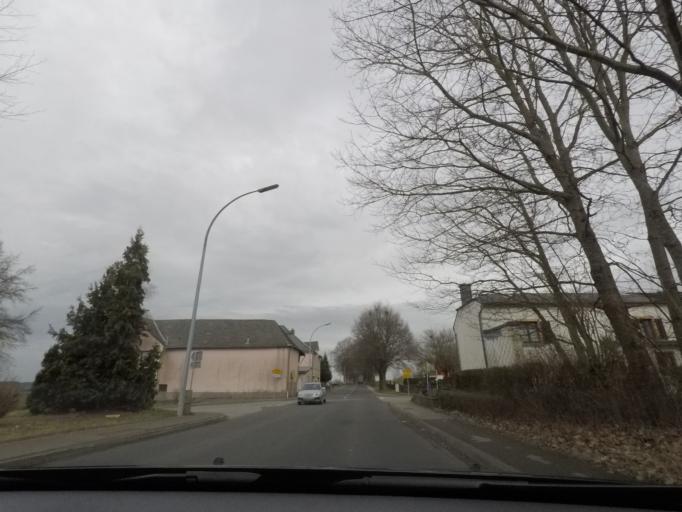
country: LU
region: Diekirch
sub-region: Canton de Wiltz
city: Winseler
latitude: 50.0152
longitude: 5.8835
